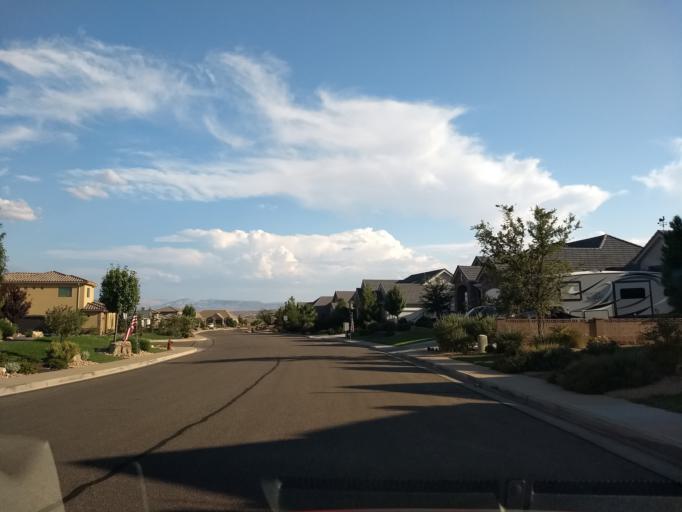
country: US
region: Utah
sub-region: Washington County
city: Saint George
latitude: 37.1051
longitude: -113.5499
